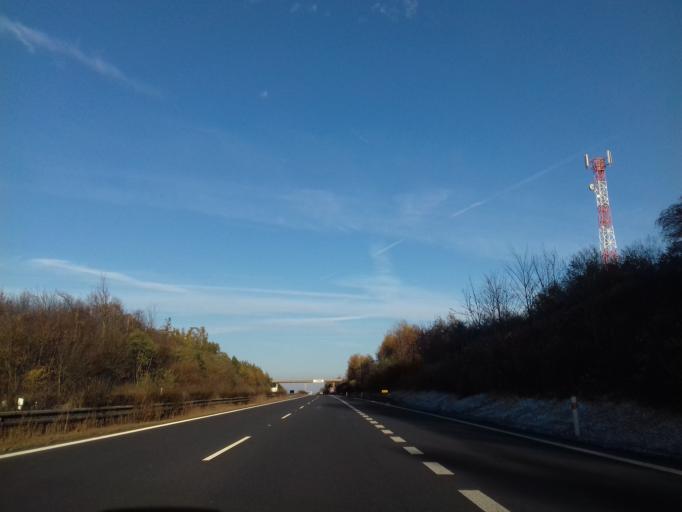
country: CZ
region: Central Bohemia
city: Zebrak
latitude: 49.8547
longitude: 13.8724
